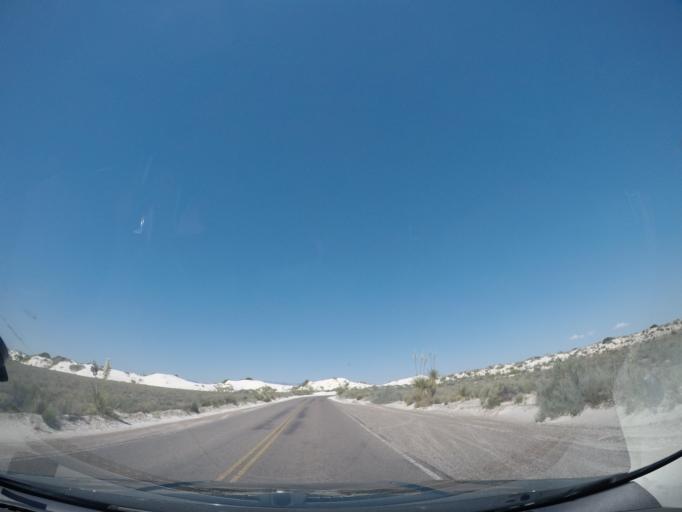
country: US
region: New Mexico
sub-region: Otero County
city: Holloman Air Force Base
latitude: 32.7952
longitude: -106.2135
